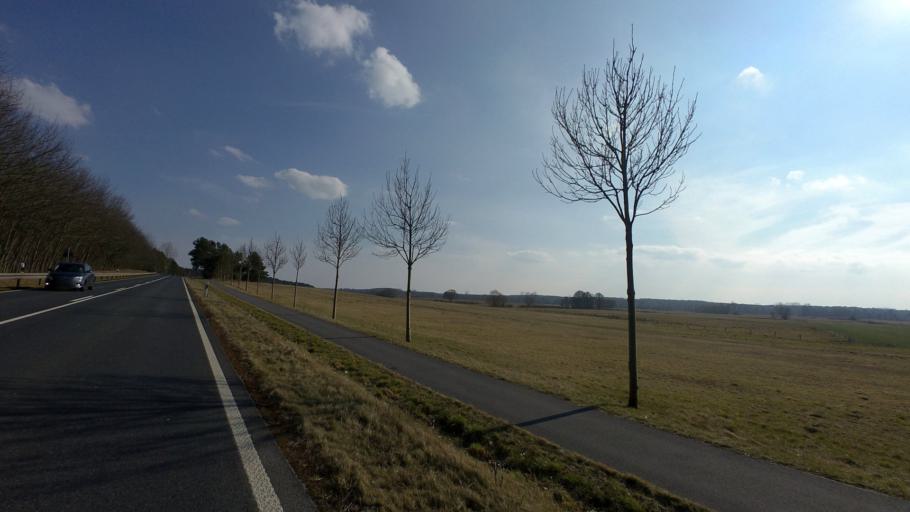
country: DE
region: Brandenburg
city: Beelitz
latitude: 52.2307
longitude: 13.0314
